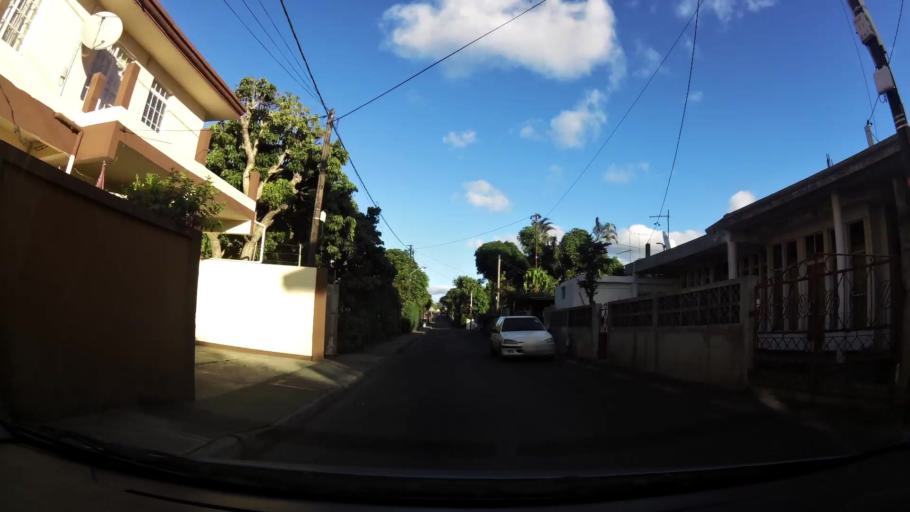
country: MU
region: Plaines Wilhems
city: Quatre Bornes
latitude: -20.2417
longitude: 57.4656
